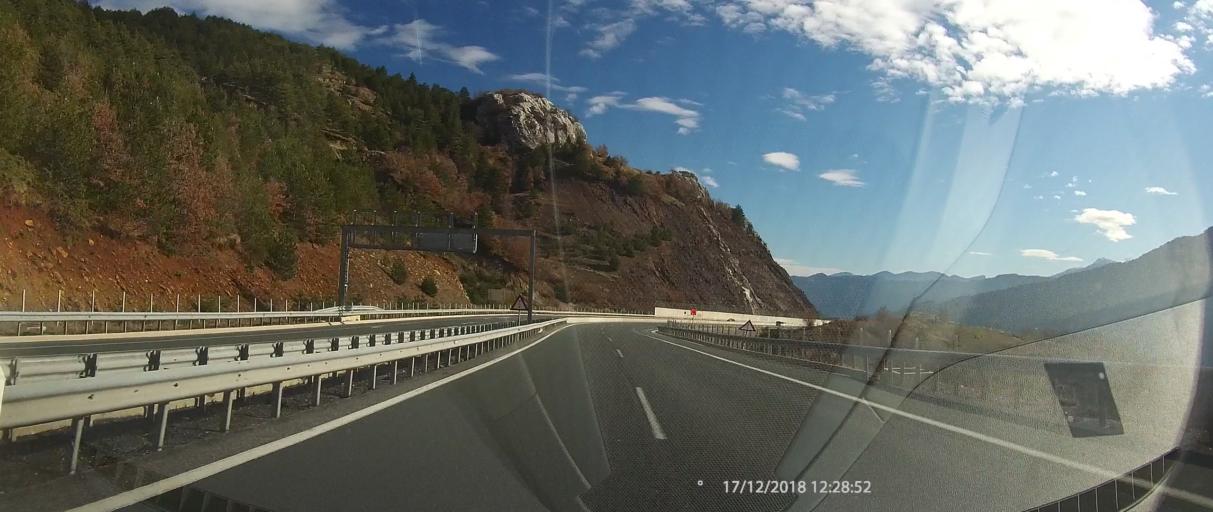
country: GR
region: Epirus
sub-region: Nomos Ioanninon
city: Metsovo
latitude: 39.7870
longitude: 21.2821
